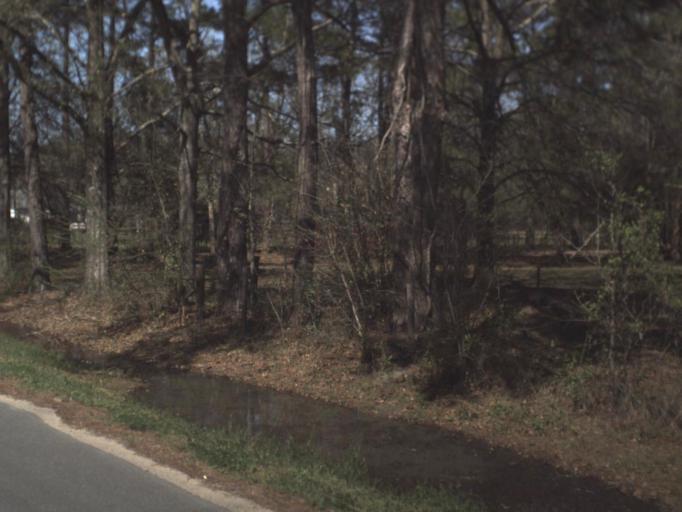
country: US
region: Florida
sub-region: Gadsden County
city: Gretna
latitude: 30.6226
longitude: -84.6663
